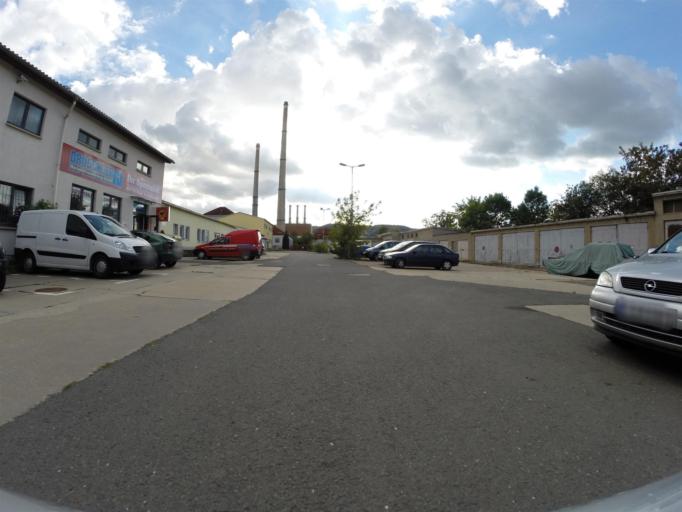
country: DE
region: Thuringia
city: Jena
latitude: 50.8997
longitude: 11.5922
